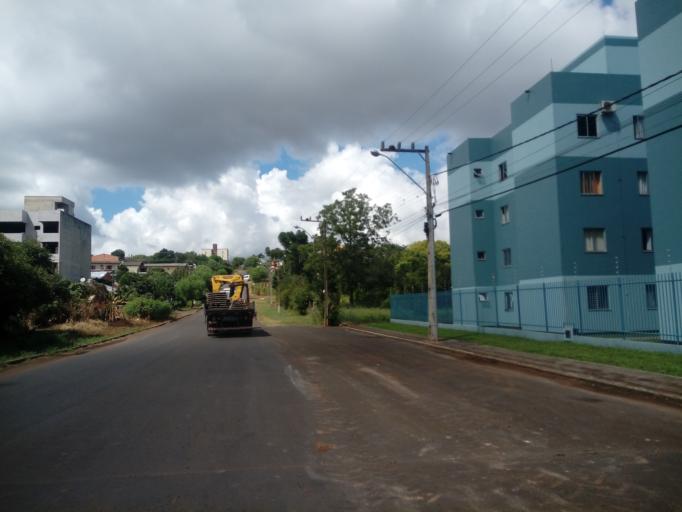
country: BR
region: Santa Catarina
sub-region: Chapeco
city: Chapeco
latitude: -27.0874
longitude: -52.6066
